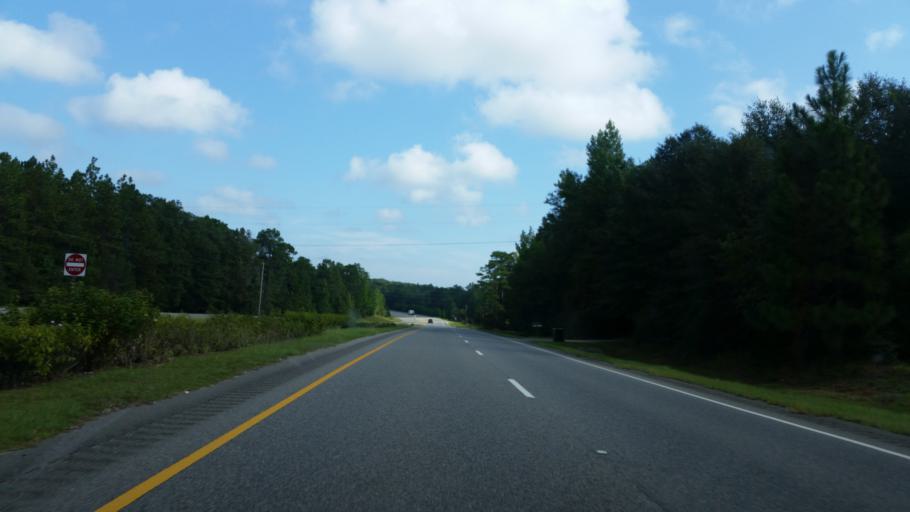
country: US
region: Alabama
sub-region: Baldwin County
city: Bay Minette
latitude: 30.9470
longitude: -87.7634
